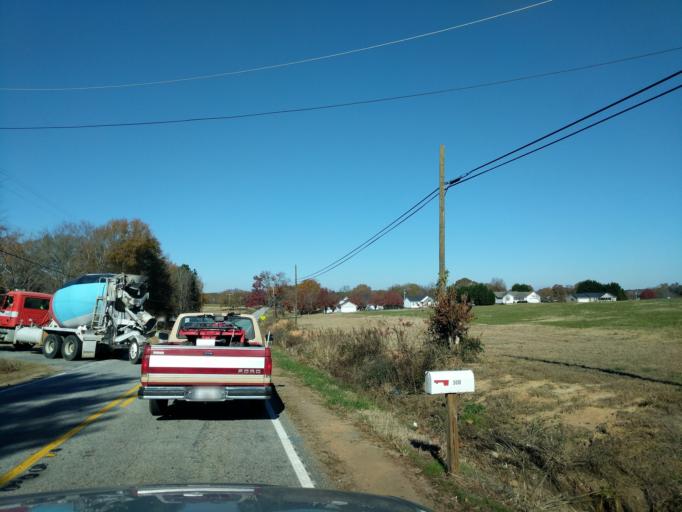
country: US
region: South Carolina
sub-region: Spartanburg County
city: Inman Mills
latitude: 35.0160
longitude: -82.1827
